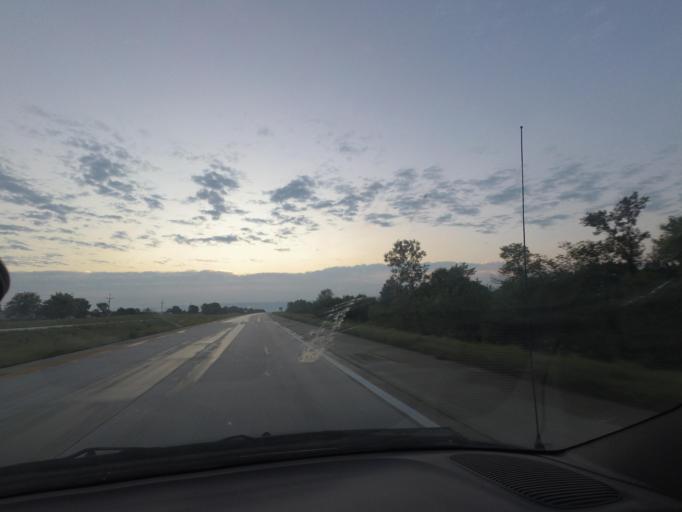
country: US
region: Missouri
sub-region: Macon County
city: Macon
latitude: 39.7606
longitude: -92.5809
